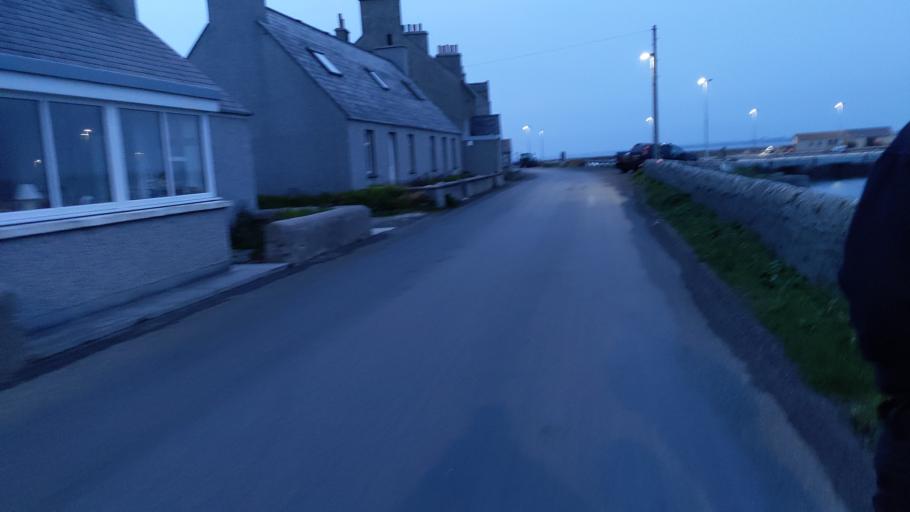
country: GB
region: Scotland
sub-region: Orkney Islands
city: Kirkwall
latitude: 59.3247
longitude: -2.9763
